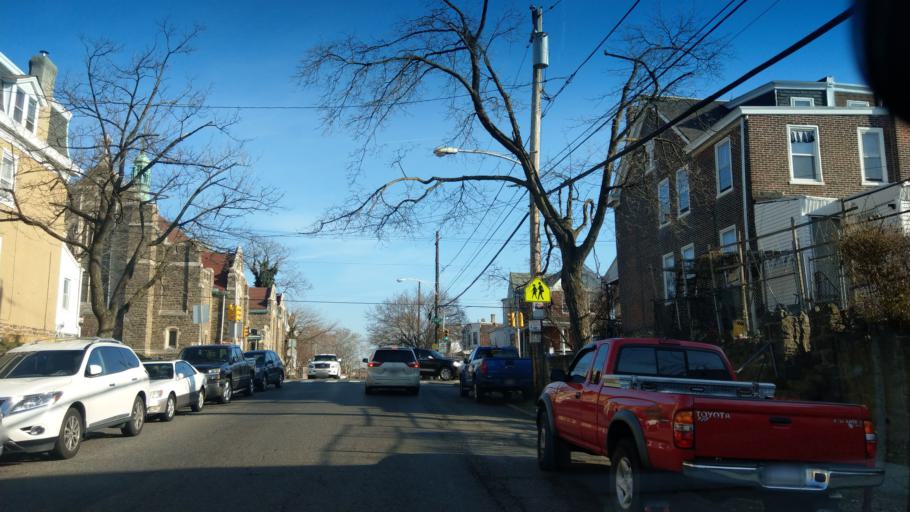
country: US
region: Pennsylvania
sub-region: Montgomery County
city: Rockledge
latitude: 40.0308
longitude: -75.1230
